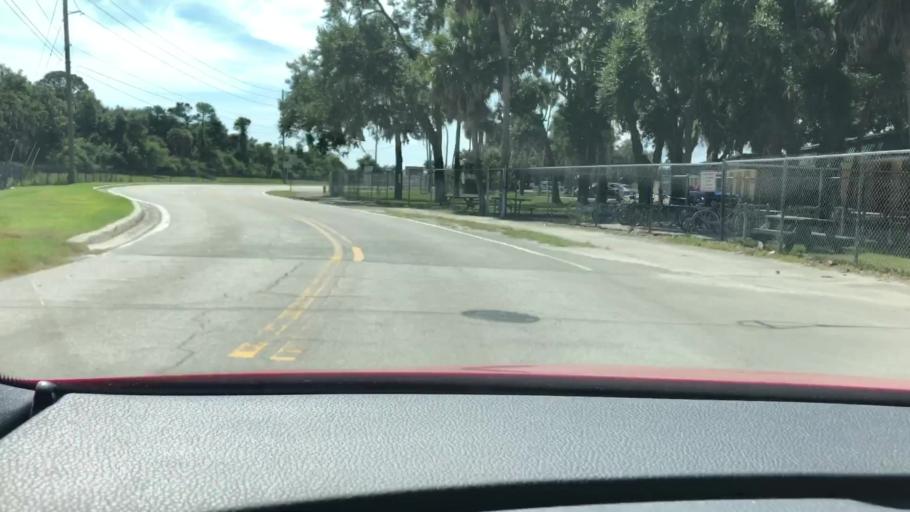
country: US
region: Florida
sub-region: Volusia County
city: New Smyrna Beach
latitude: 29.0061
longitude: -80.9235
